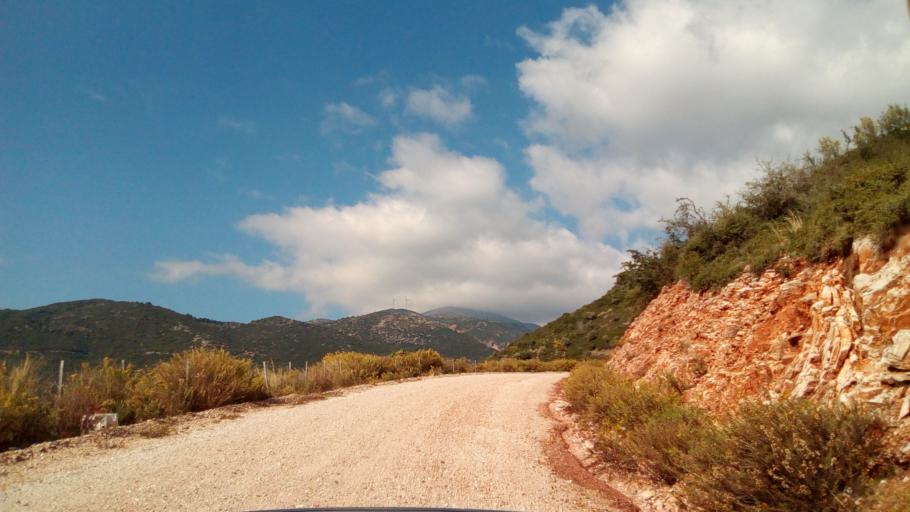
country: GR
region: West Greece
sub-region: Nomos Aitolias kai Akarnanias
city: Nafpaktos
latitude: 38.4139
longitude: 21.8471
